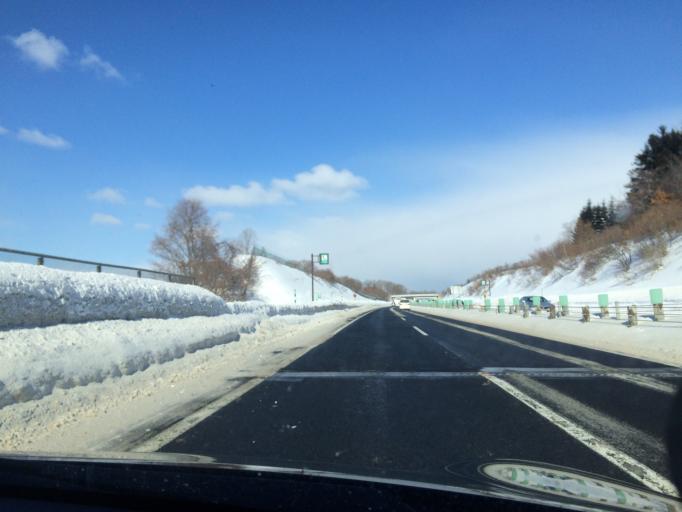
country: JP
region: Hokkaido
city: Kitahiroshima
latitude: 42.8797
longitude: 141.5509
